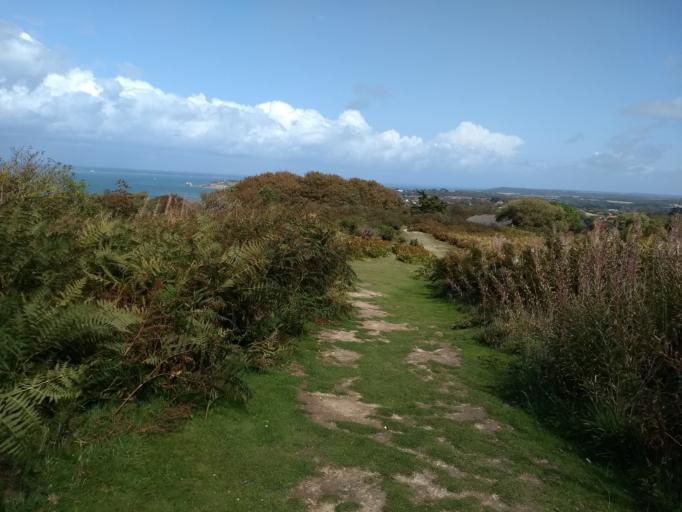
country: GB
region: England
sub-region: Isle of Wight
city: Totland
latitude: 50.6733
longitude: -1.5542
